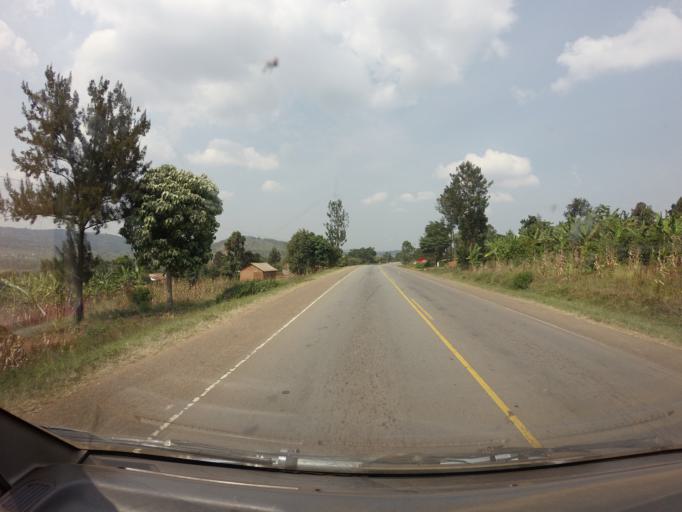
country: UG
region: Central Region
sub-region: Lwengo District
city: Lwengo
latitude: -0.3804
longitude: 31.3004
